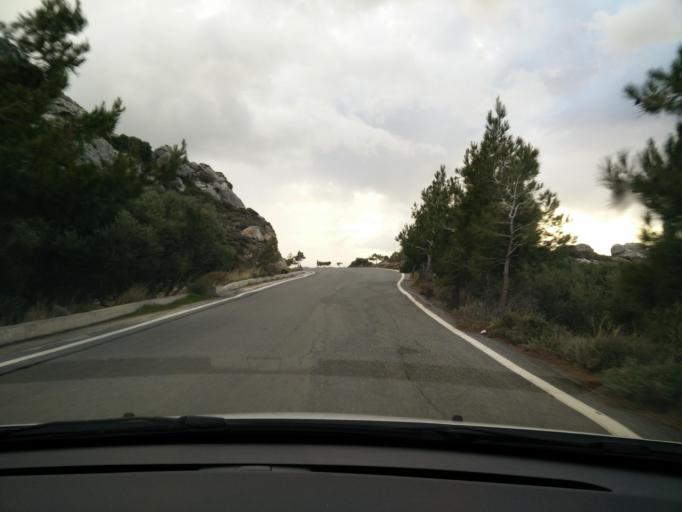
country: GR
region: Crete
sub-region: Nomos Lasithiou
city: Gra Liyia
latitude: 35.0735
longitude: 25.7037
